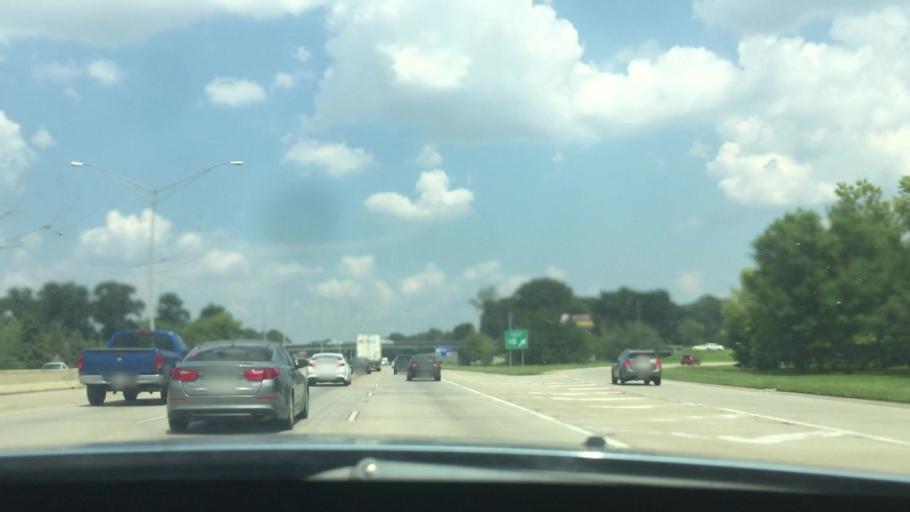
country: US
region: Louisiana
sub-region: East Baton Rouge Parish
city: Westminster
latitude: 30.4173
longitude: -91.1007
